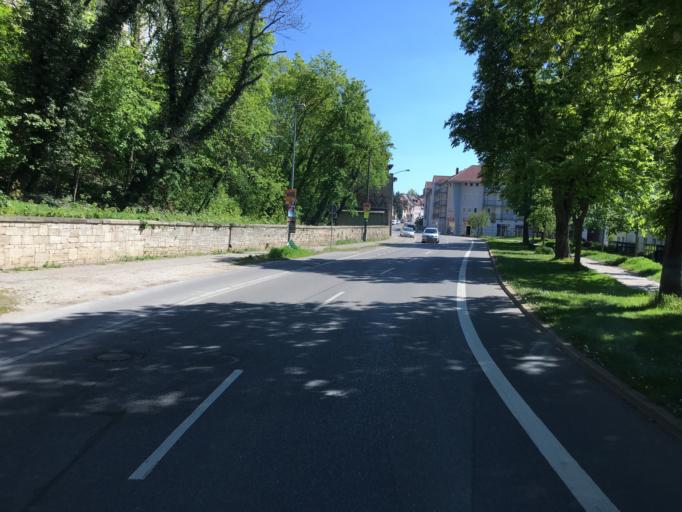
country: DE
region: Saxony-Anhalt
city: Naumburg
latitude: 51.1560
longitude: 11.7997
